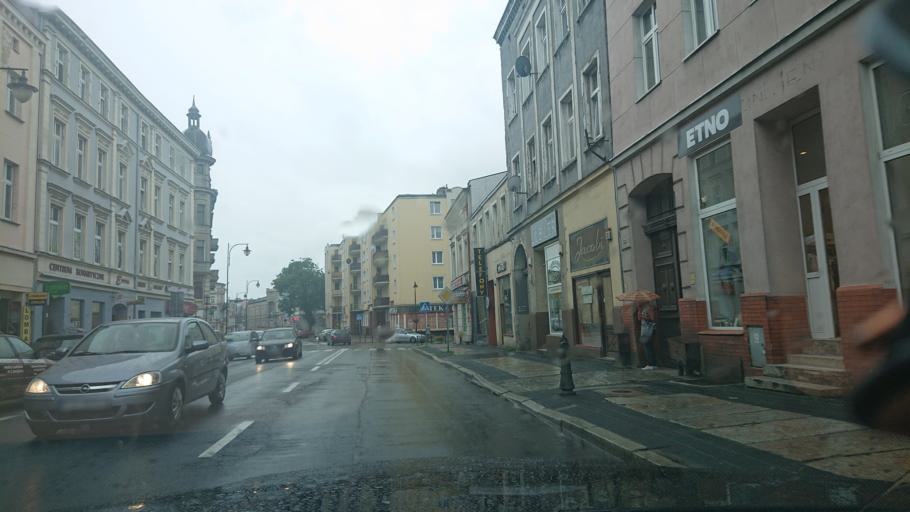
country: PL
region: Greater Poland Voivodeship
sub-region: Powiat gnieznienski
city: Gniezno
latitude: 52.5355
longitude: 17.5989
